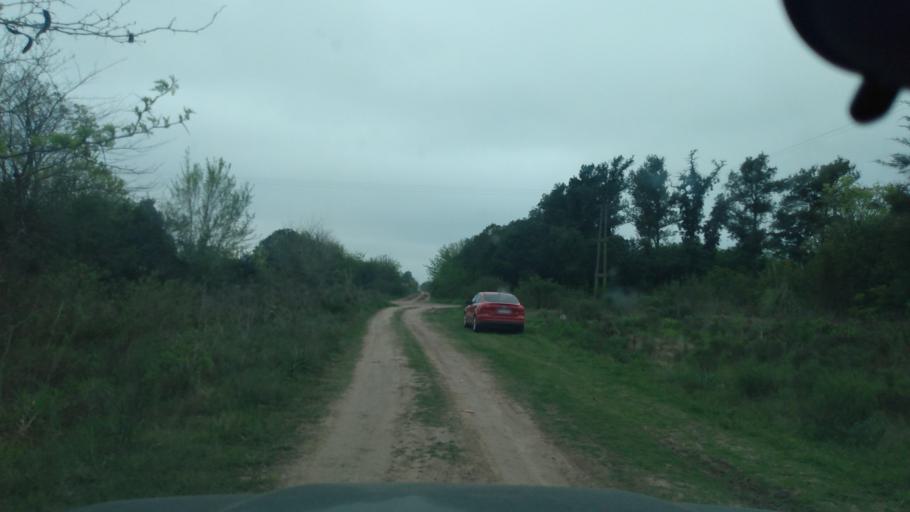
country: AR
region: Buenos Aires
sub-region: Partido de Lujan
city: Lujan
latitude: -34.5405
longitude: -59.2060
